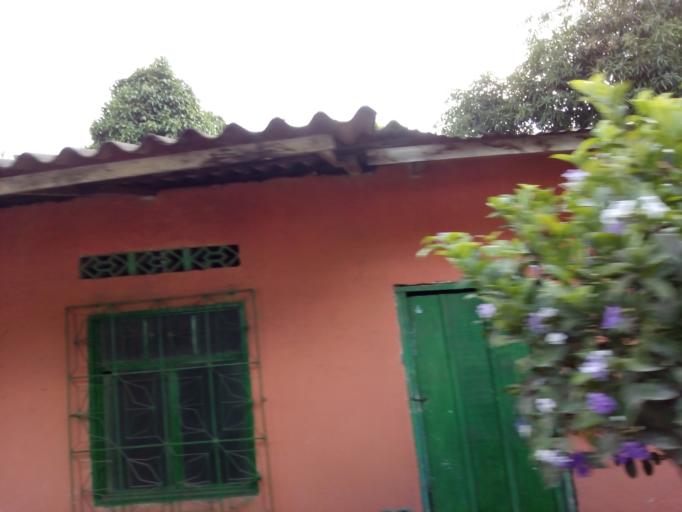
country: CO
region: Boyaca
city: Puerto Boyaca
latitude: 5.9029
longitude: -74.3697
